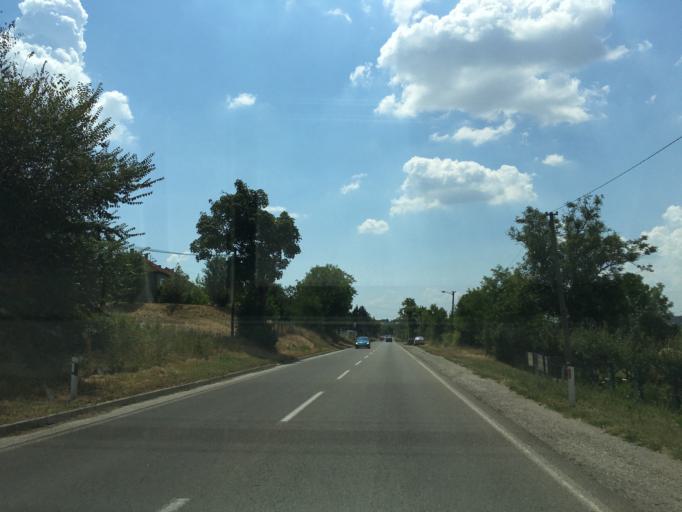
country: RS
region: Central Serbia
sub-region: Belgrade
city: Mladenovac
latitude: 44.4823
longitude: 20.6599
